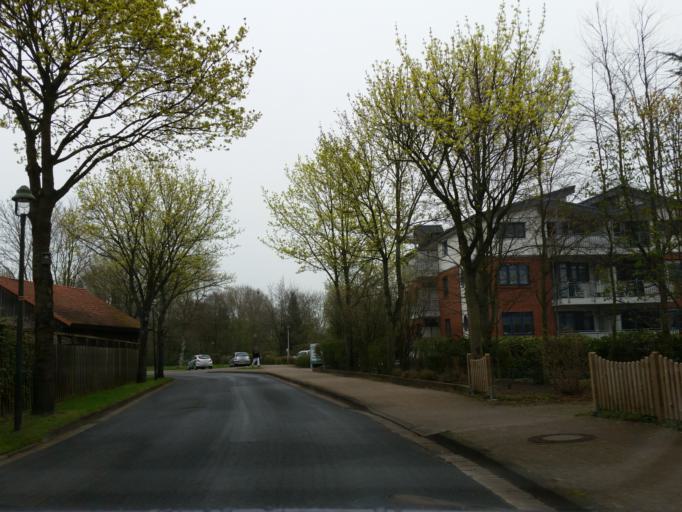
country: DE
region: Lower Saxony
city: Bremervorde
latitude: 53.4904
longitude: 9.1463
